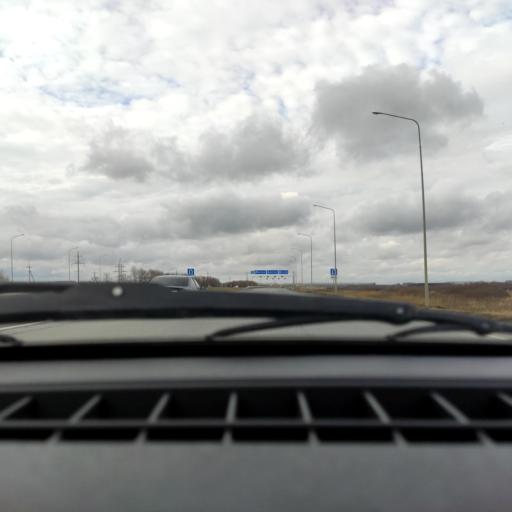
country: RU
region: Bashkortostan
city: Asanovo
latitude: 54.9067
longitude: 55.6115
